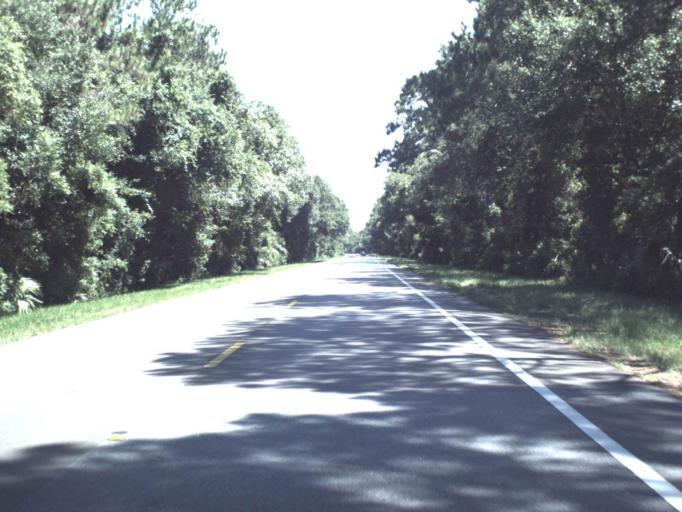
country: US
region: Florida
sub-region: Duval County
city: Atlantic Beach
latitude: 30.4732
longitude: -81.4399
